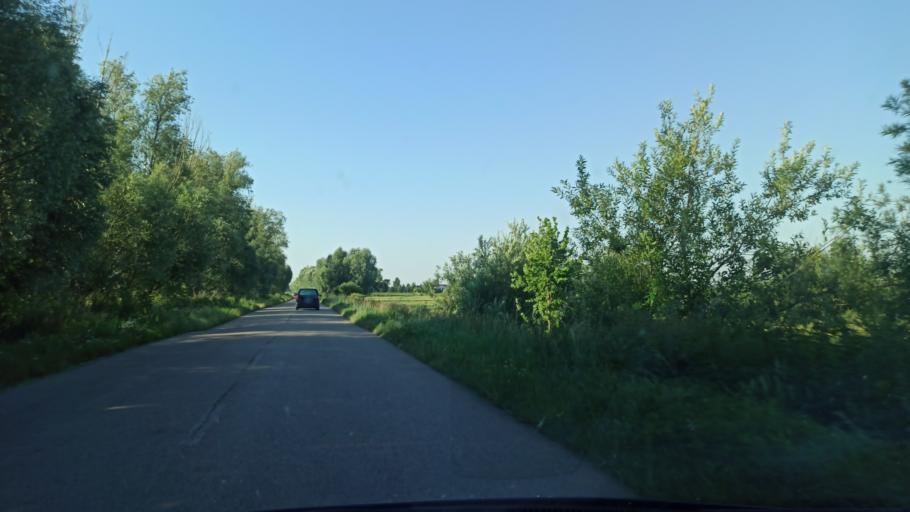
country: PL
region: Warmian-Masurian Voivodeship
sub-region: Powiat elblaski
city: Elblag
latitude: 54.1729
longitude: 19.3311
